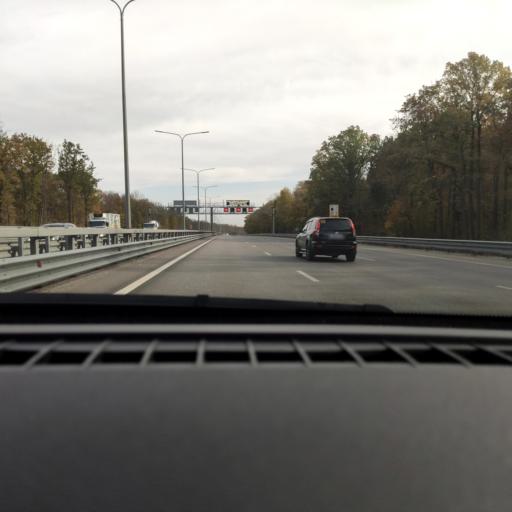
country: RU
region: Voronezj
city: Podgornoye
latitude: 51.8346
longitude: 39.2311
